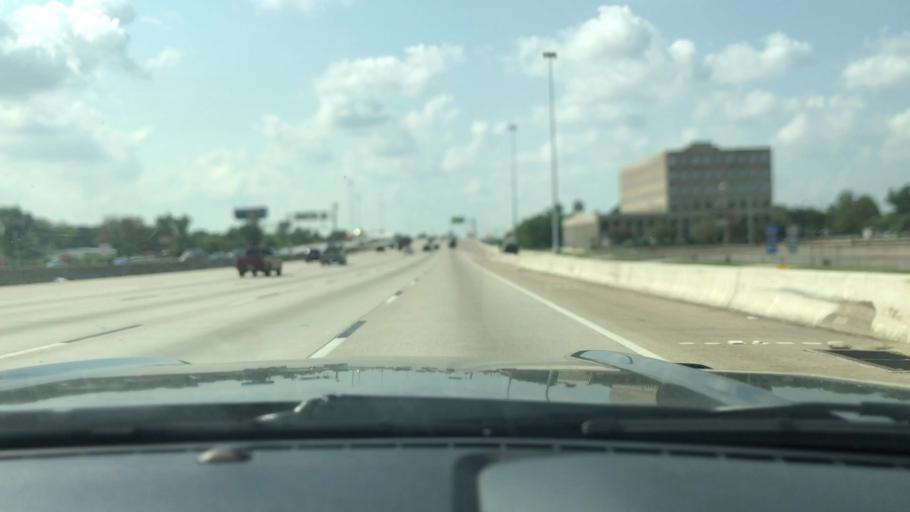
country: US
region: Texas
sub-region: Harris County
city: Houston
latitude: 29.8460
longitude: -95.3339
